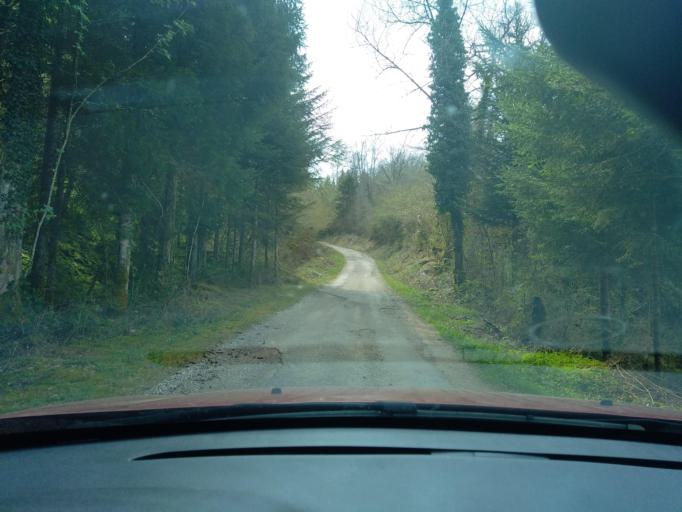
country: FR
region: Franche-Comte
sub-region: Departement du Jura
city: Moirans-en-Montagne
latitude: 46.4519
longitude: 5.7348
